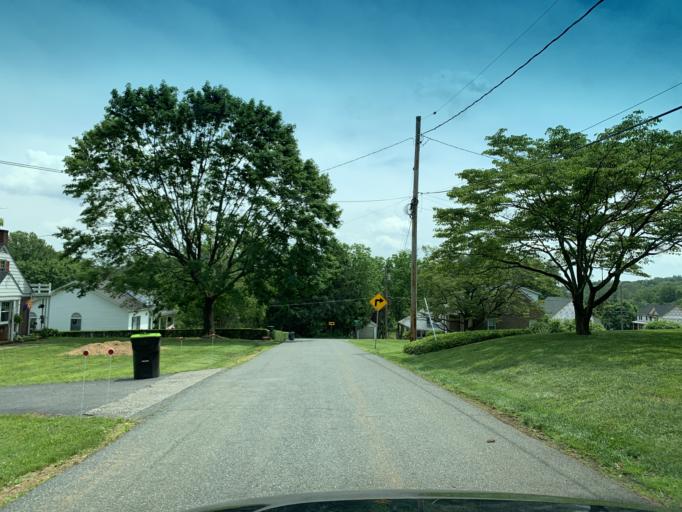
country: US
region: Maryland
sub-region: Harford County
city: North Bel Air
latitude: 39.5526
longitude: -76.3504
